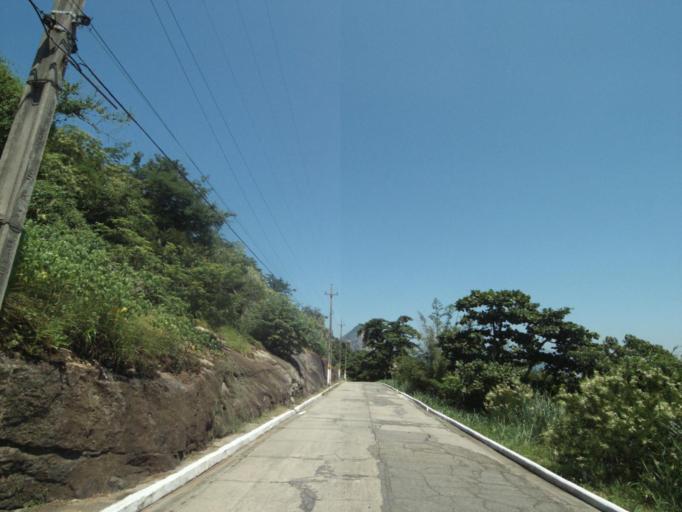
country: BR
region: Rio de Janeiro
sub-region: Niteroi
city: Niteroi
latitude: -22.9368
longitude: -43.1286
